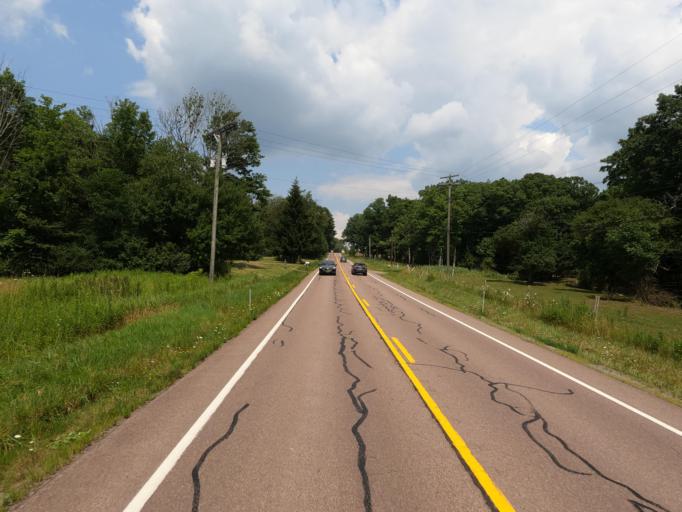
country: US
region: Maryland
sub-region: Allegany County
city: Westernport
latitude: 39.6298
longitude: -79.2139
